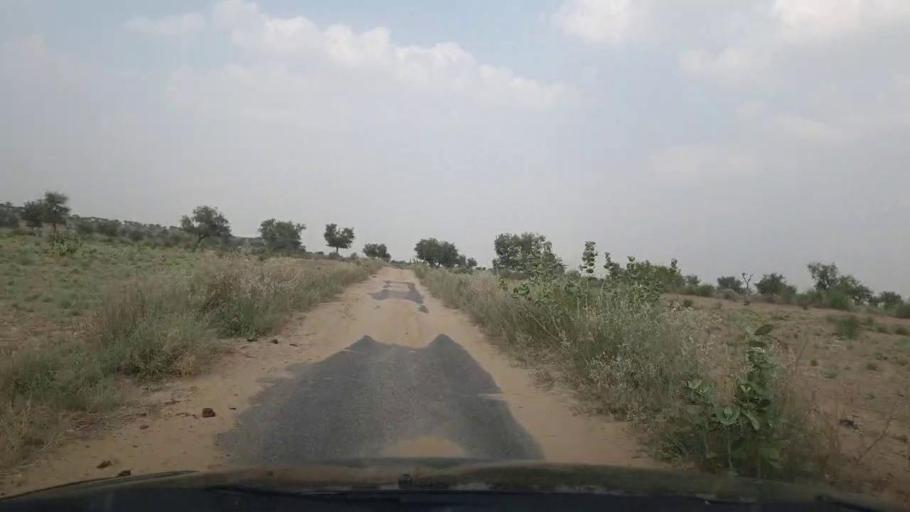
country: PK
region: Sindh
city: Islamkot
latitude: 24.9112
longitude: 70.5606
